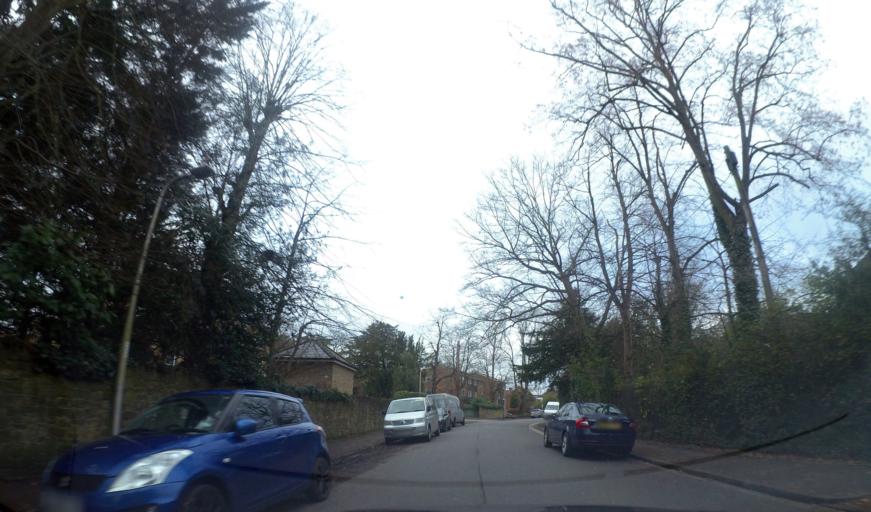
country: GB
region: England
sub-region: Reading
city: Reading
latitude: 51.4487
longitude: -0.9953
